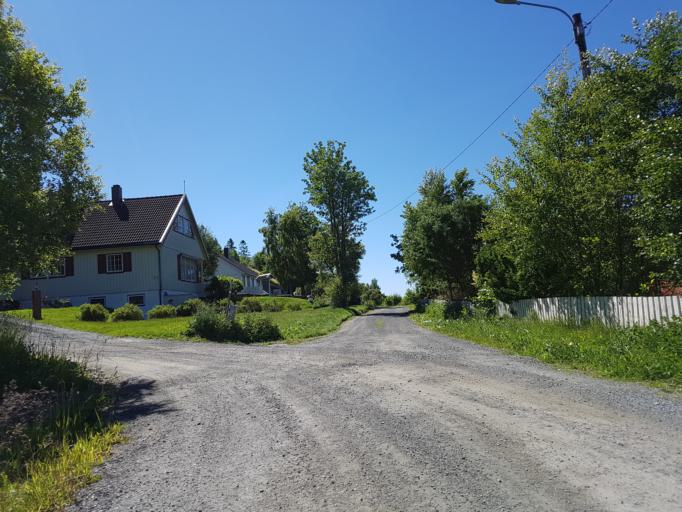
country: NO
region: Sor-Trondelag
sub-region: Skaun
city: Borsa
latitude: 63.4326
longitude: 10.1845
